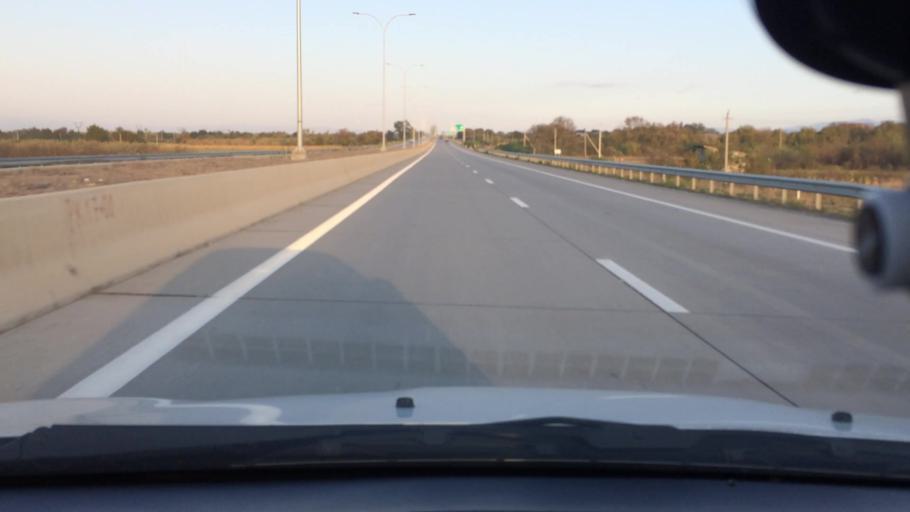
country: GE
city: Agara
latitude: 42.0273
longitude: 43.9615
